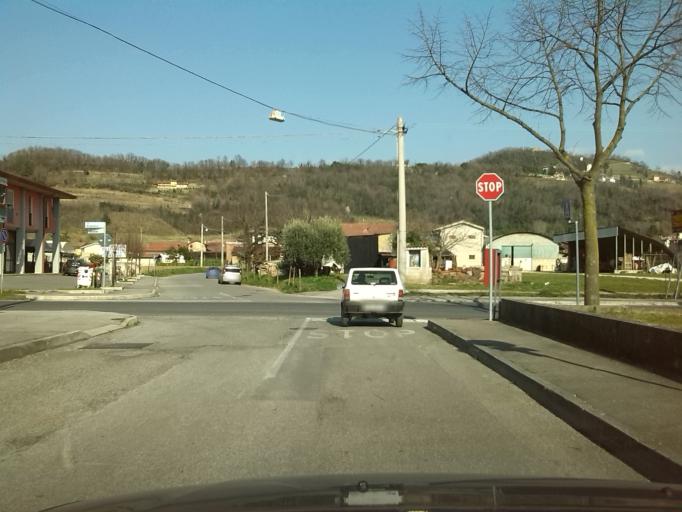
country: IT
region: Friuli Venezia Giulia
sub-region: Provincia di Gorizia
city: Cormons
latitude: 45.9650
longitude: 13.4606
